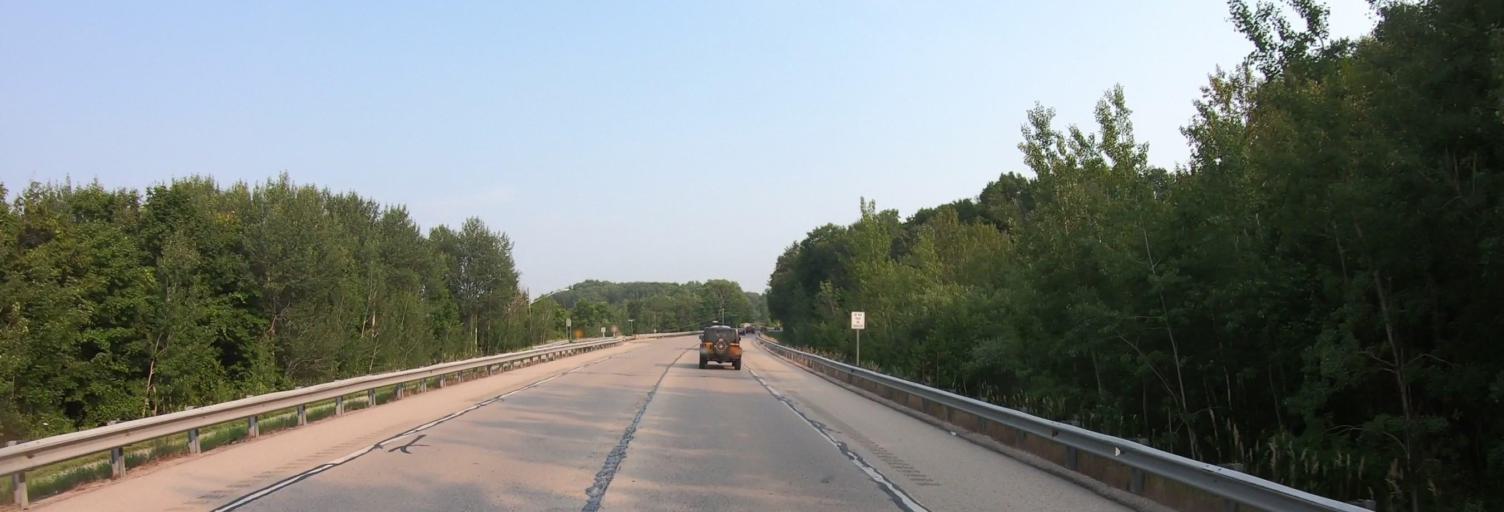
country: US
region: Michigan
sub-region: Charlevoix County
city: Charlevoix
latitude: 45.3660
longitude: -85.1233
